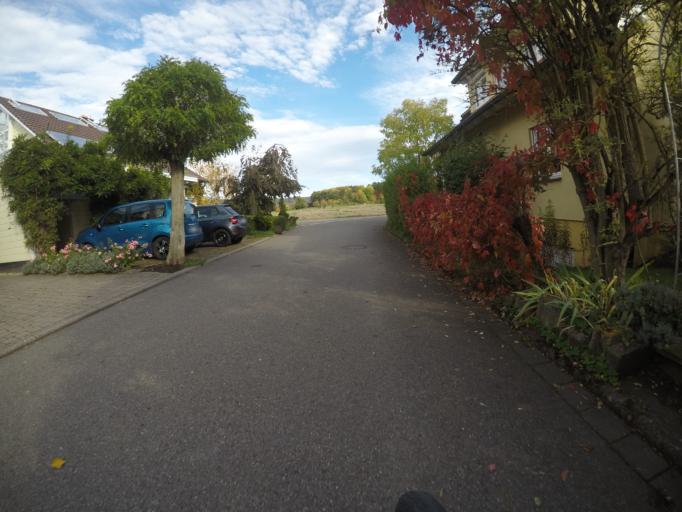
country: DE
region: Baden-Wuerttemberg
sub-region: Regierungsbezirk Stuttgart
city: Herrenberg
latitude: 48.5815
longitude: 8.8788
